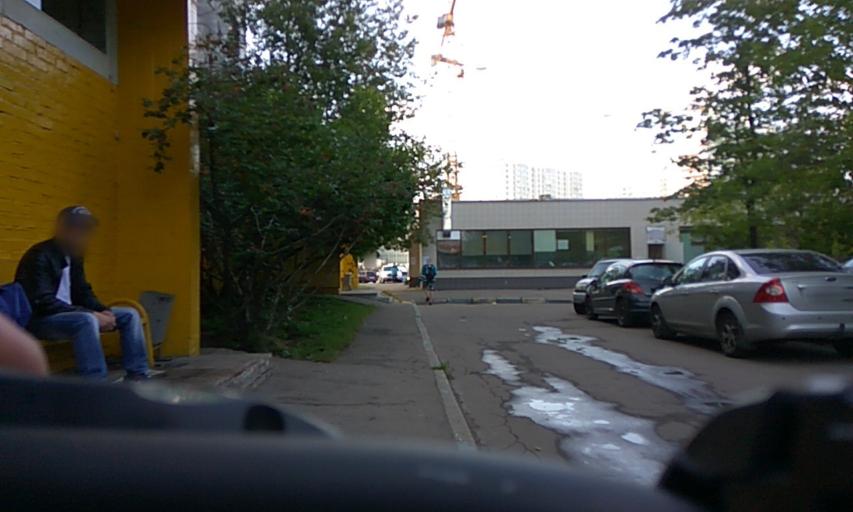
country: RU
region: Moscow
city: Kolomenskoye
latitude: 55.6778
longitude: 37.6962
